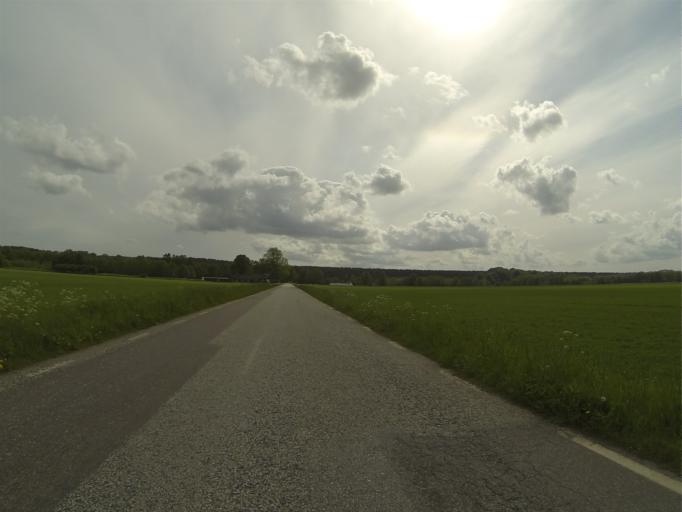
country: SE
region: Skane
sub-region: Sjobo Kommun
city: Blentarp
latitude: 55.6658
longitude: 13.6208
